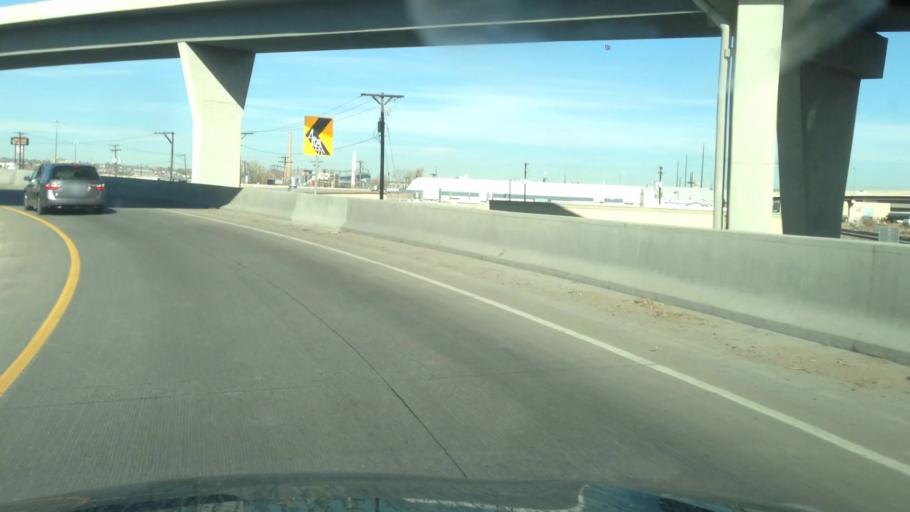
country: US
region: Colorado
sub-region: Denver County
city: Denver
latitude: 39.7260
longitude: -105.0113
